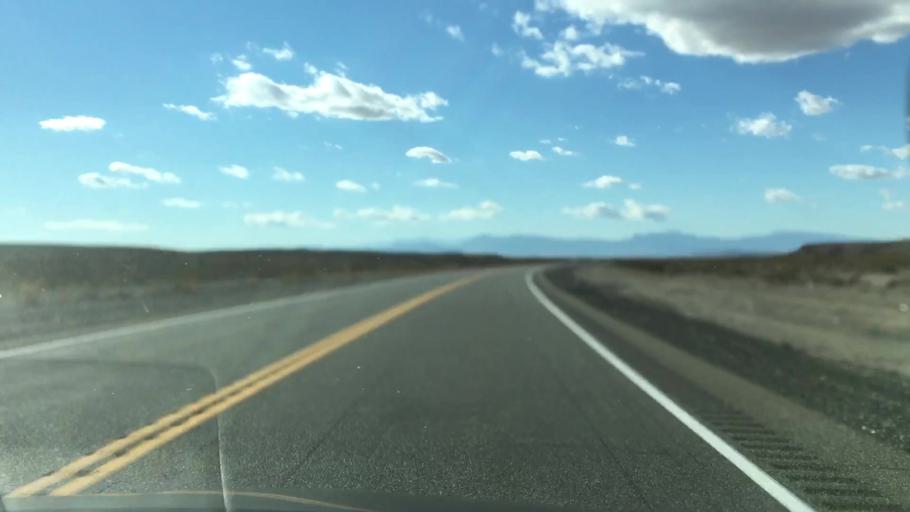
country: US
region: Nevada
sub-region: Nye County
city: Pahrump
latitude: 36.5622
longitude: -116.0901
